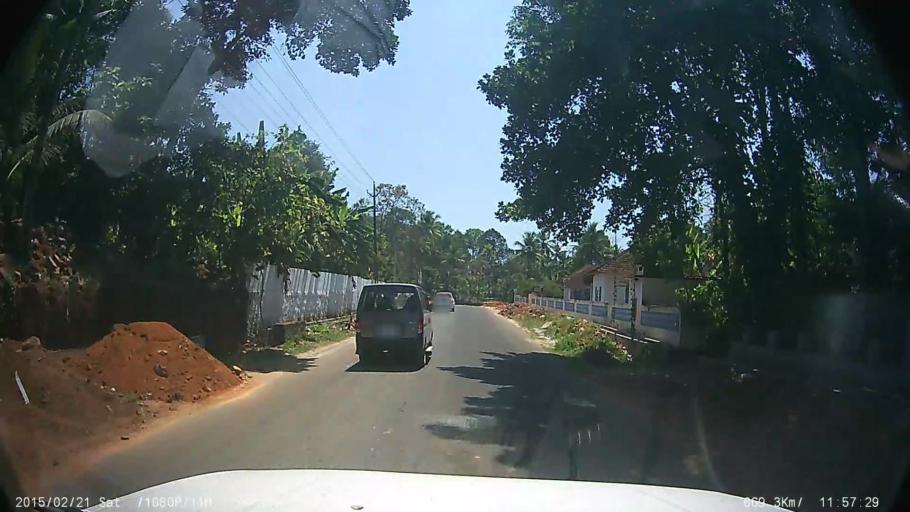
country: IN
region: Kerala
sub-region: Kottayam
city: Lalam
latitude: 9.7392
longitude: 76.6905
